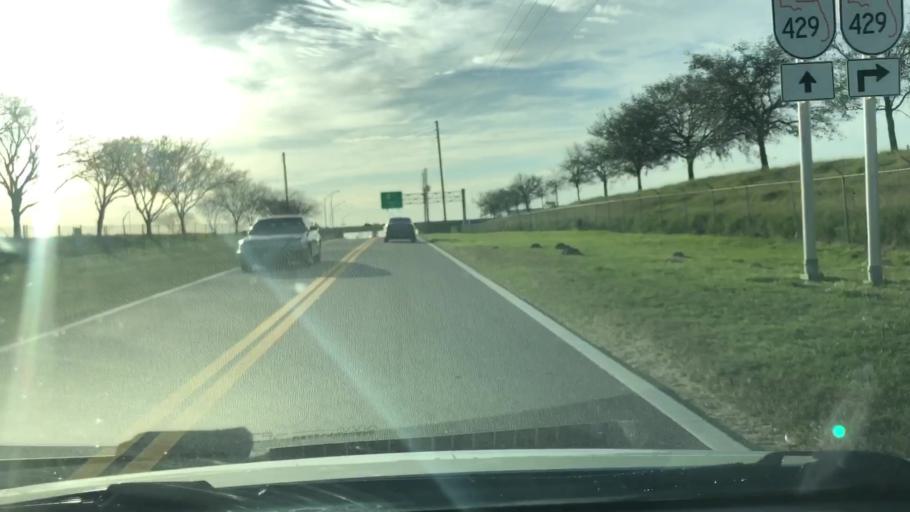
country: US
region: Florida
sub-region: Orange County
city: Oakland
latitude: 28.4490
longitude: -81.6385
